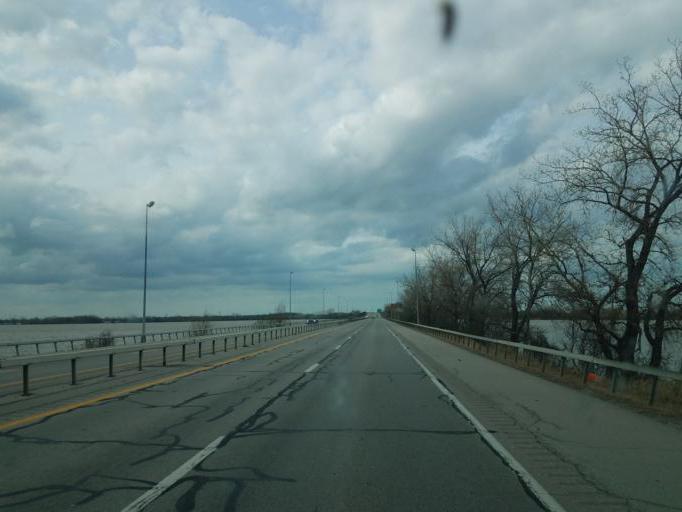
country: US
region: Ohio
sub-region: Ottawa County
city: Port Clinton
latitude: 41.4890
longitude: -82.8355
